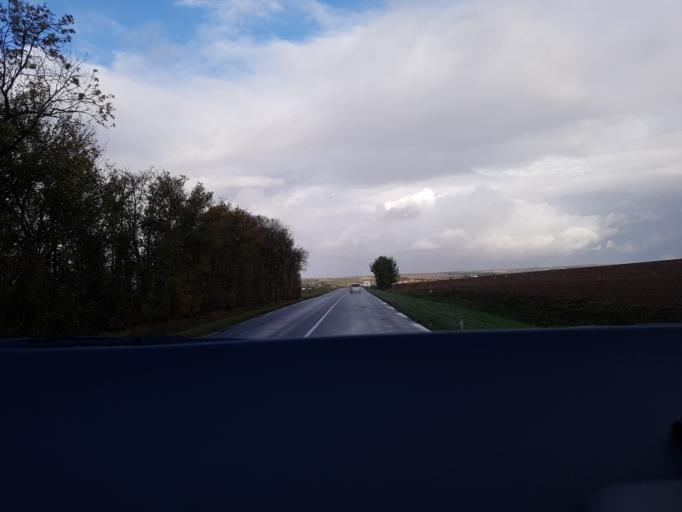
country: FR
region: Poitou-Charentes
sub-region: Departement de la Charente-Maritime
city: Aulnay
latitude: 46.0122
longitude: -0.3709
